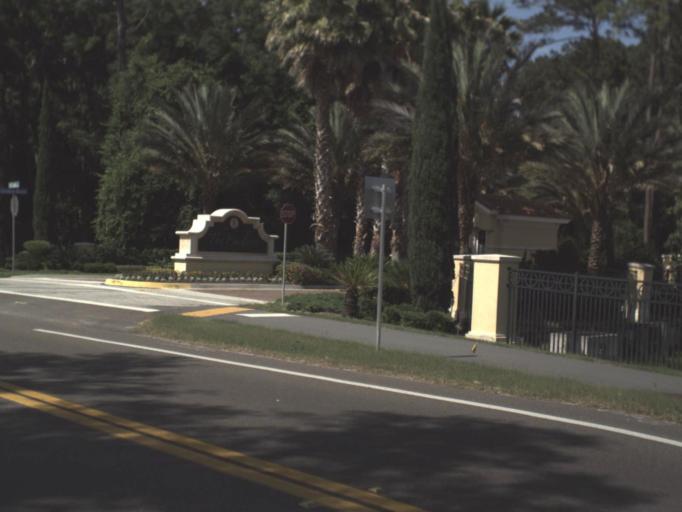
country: US
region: Florida
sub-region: Nassau County
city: Fernandina Beach
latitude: 30.5816
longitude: -81.4543
